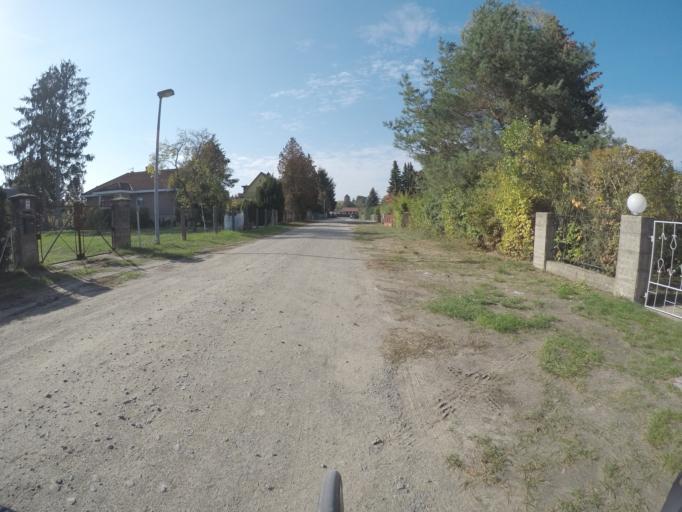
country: DE
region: Brandenburg
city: Oranienburg
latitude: 52.7249
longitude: 13.2391
